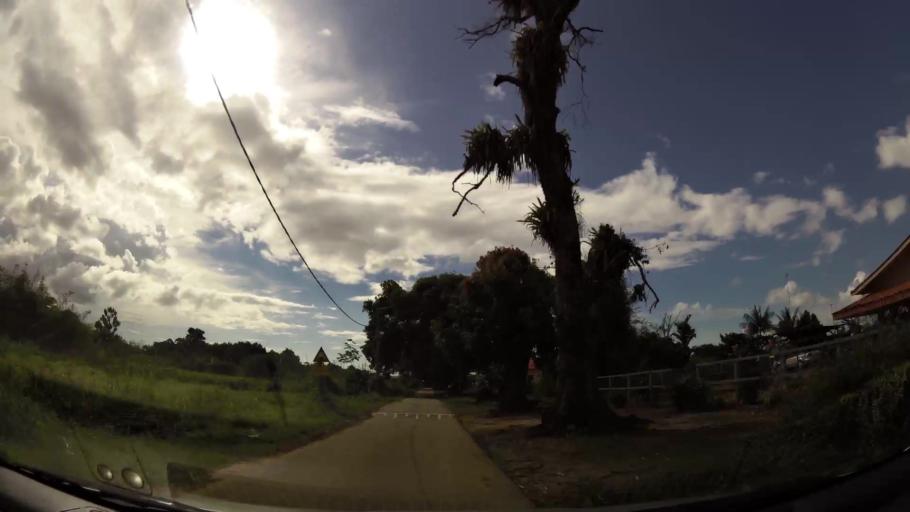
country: SR
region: Paramaribo
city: Paramaribo
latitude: 5.8509
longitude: -55.1595
